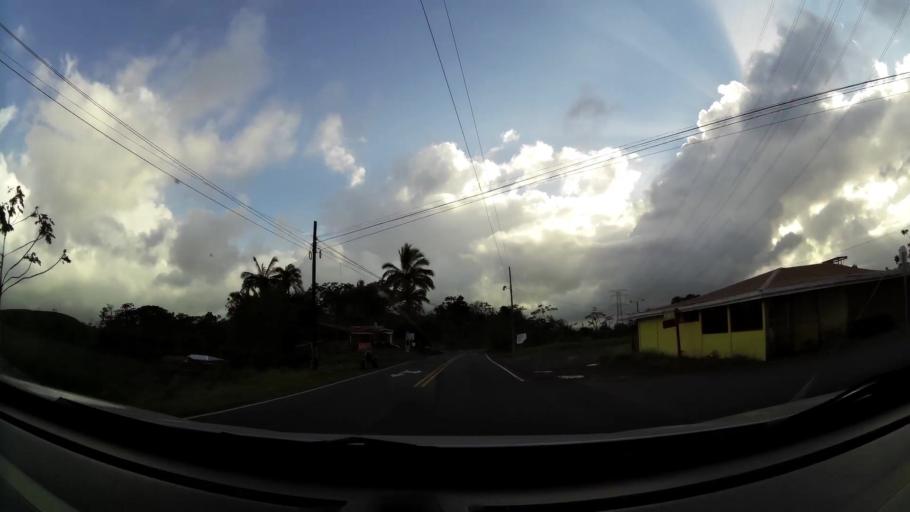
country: CR
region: Limon
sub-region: Canton de Siquirres
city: Siquirres
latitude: 10.0150
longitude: -83.5642
